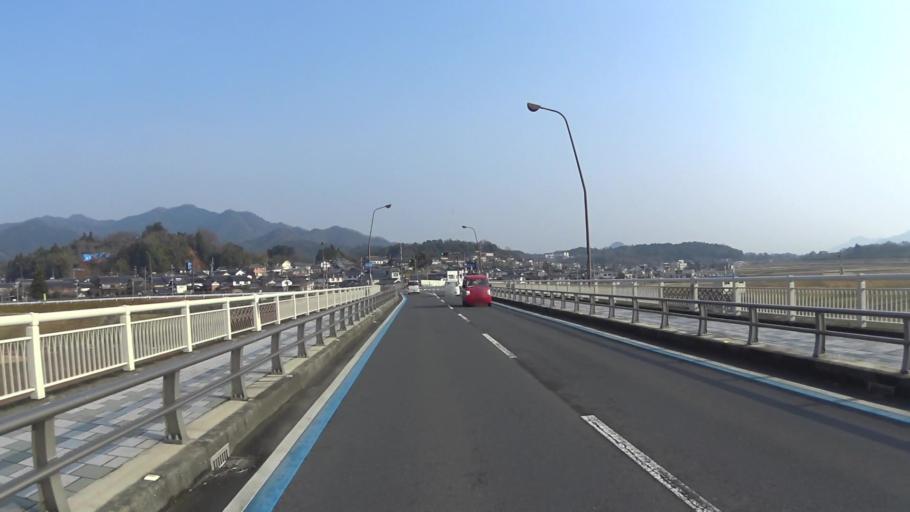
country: JP
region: Kyoto
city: Fukuchiyama
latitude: 35.3037
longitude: 135.1308
